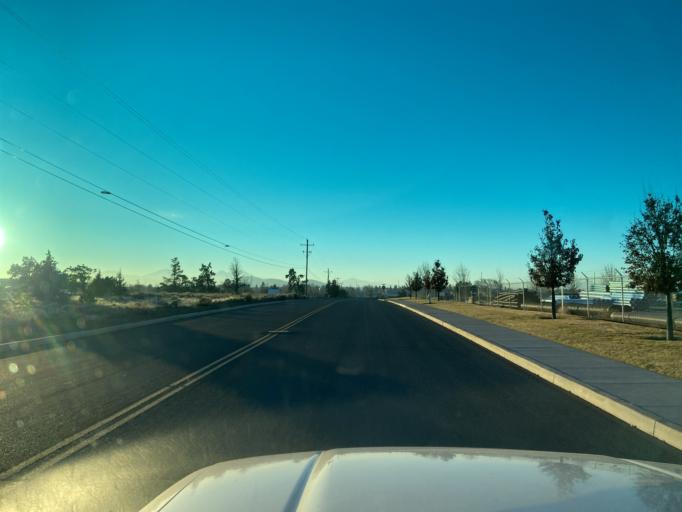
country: US
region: Oregon
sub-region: Deschutes County
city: Redmond
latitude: 44.2766
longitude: -121.1572
